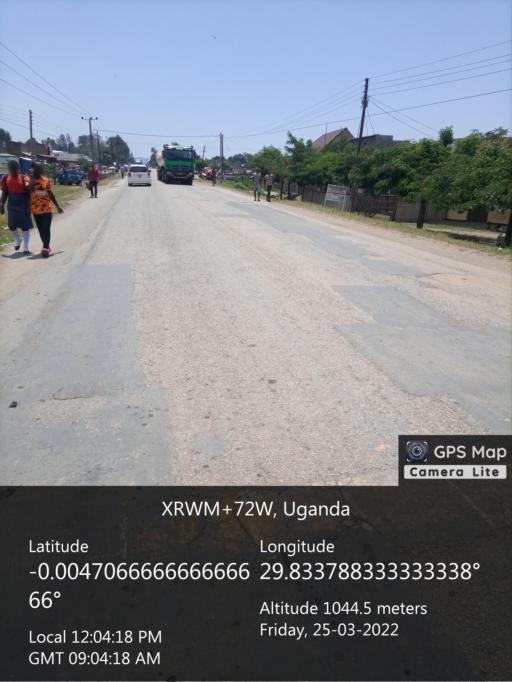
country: UG
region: Western Region
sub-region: Kasese District
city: Kilembe
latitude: -0.0047
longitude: 29.8338
